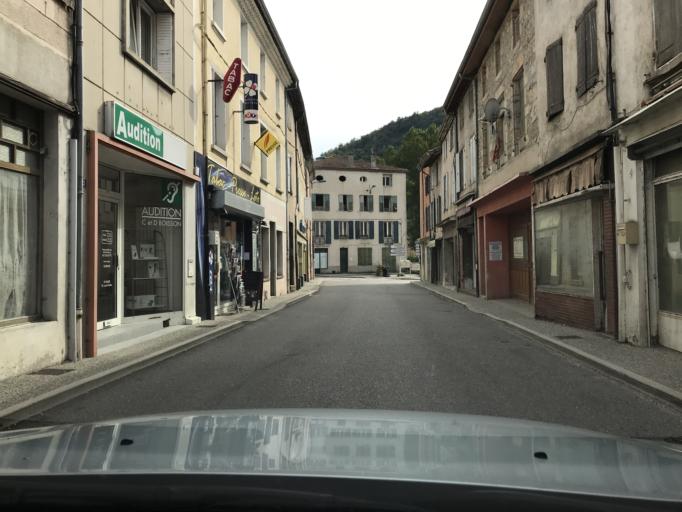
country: FR
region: Rhone-Alpes
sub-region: Departement de l'Ardeche
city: Lamastre
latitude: 44.9859
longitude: 4.5822
